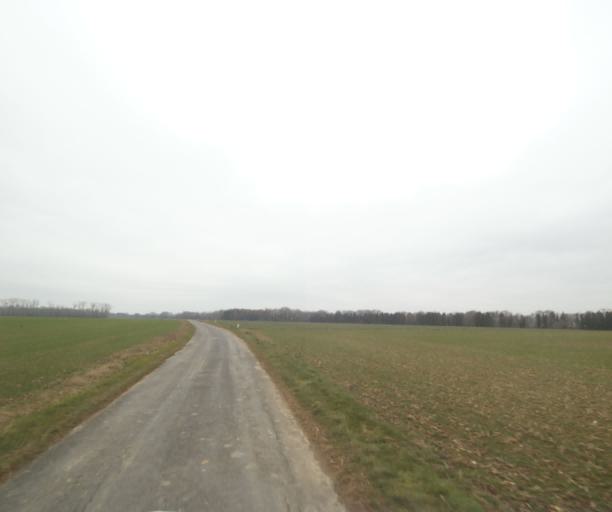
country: FR
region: Champagne-Ardenne
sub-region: Departement de la Haute-Marne
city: Villiers-en-Lieu
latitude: 48.6364
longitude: 4.8058
